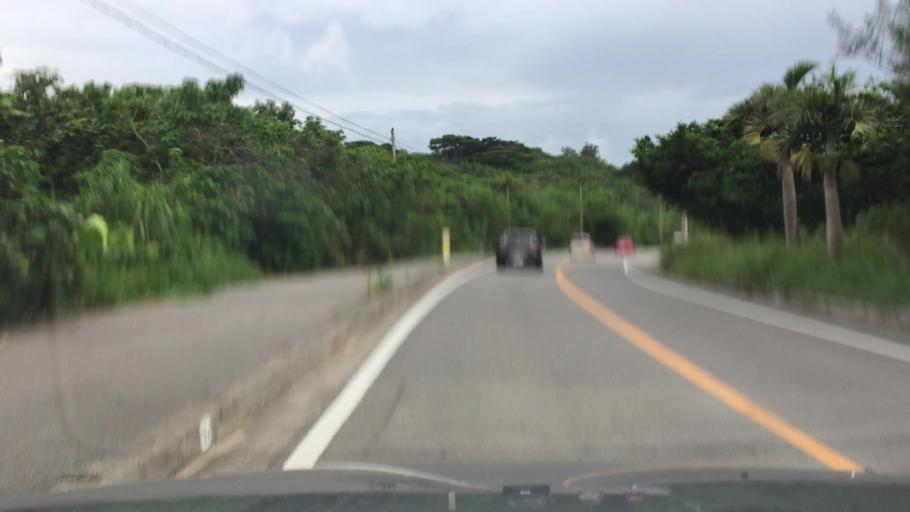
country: JP
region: Okinawa
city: Ishigaki
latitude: 24.4315
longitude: 124.1247
